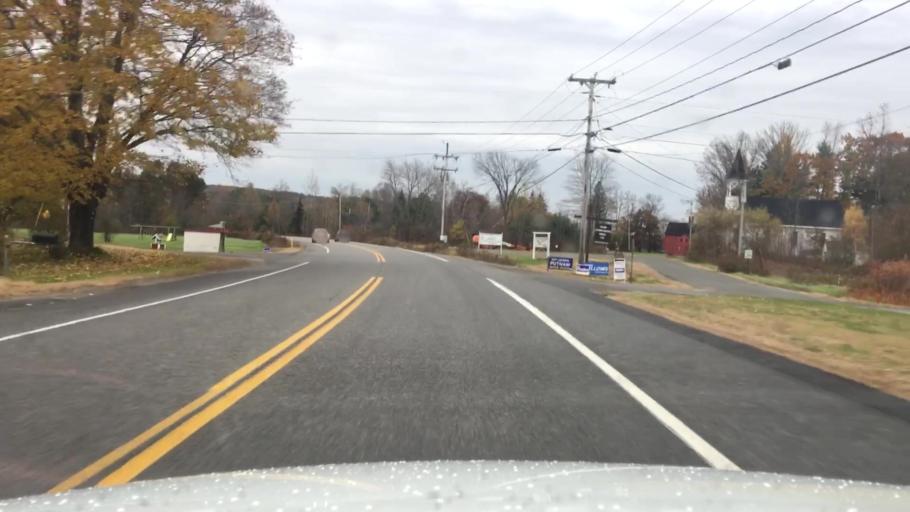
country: US
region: Maine
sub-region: Kennebec County
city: Pittston
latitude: 44.2000
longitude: -69.7535
